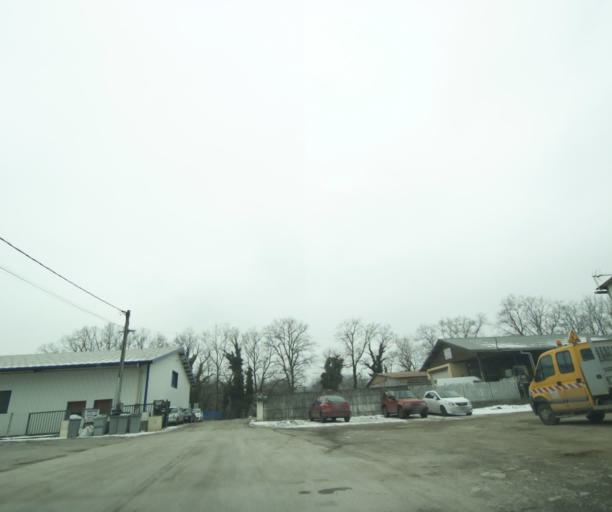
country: FR
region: Rhone-Alpes
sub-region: Departement de la Haute-Savoie
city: Reignier-Esery
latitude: 46.1304
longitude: 6.2984
